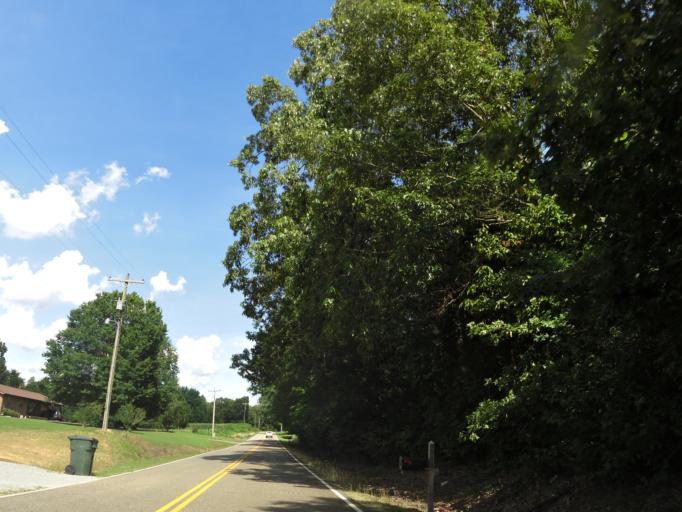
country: US
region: Tennessee
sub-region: Gibson County
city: Milan
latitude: 35.9781
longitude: -88.7315
